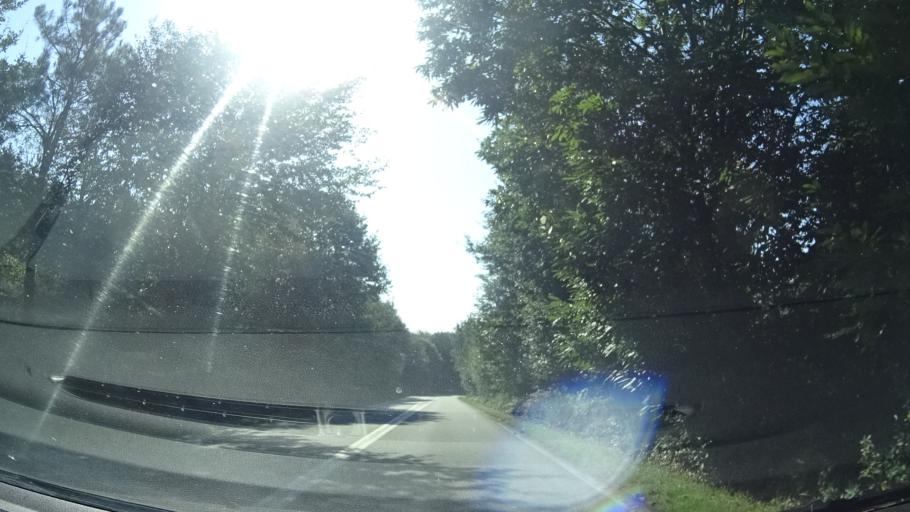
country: FR
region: Brittany
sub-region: Departement du Finistere
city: Cast
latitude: 48.1721
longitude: -4.1234
